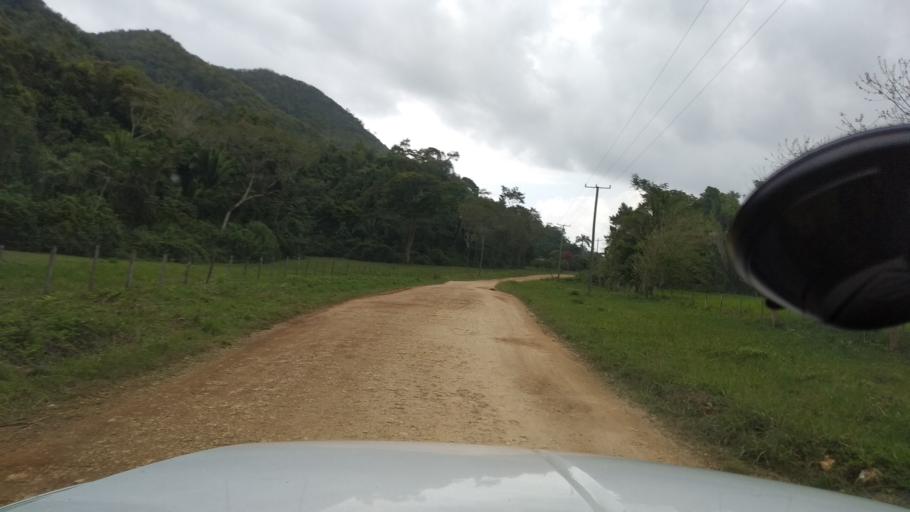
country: BZ
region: Toledo
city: Punta Gorda
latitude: 16.2108
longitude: -89.0224
